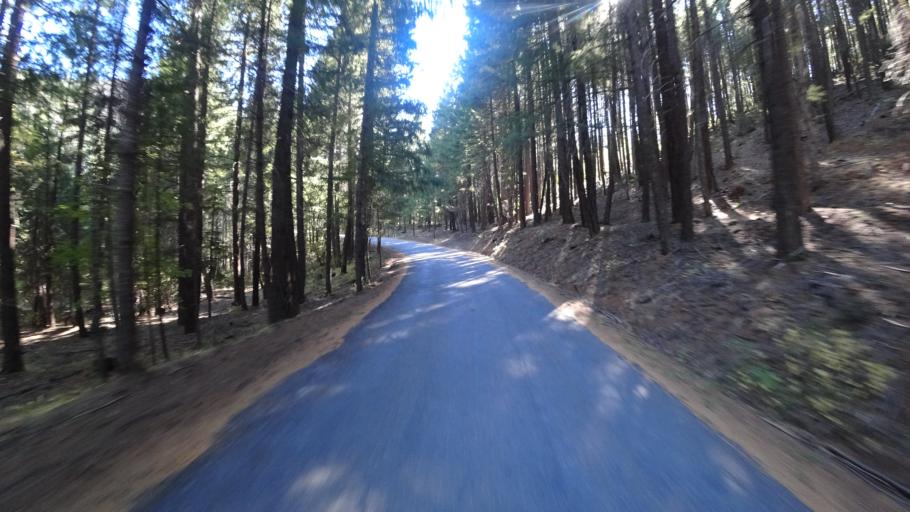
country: US
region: California
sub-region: Siskiyou County
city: Happy Camp
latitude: 41.3198
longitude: -123.0619
